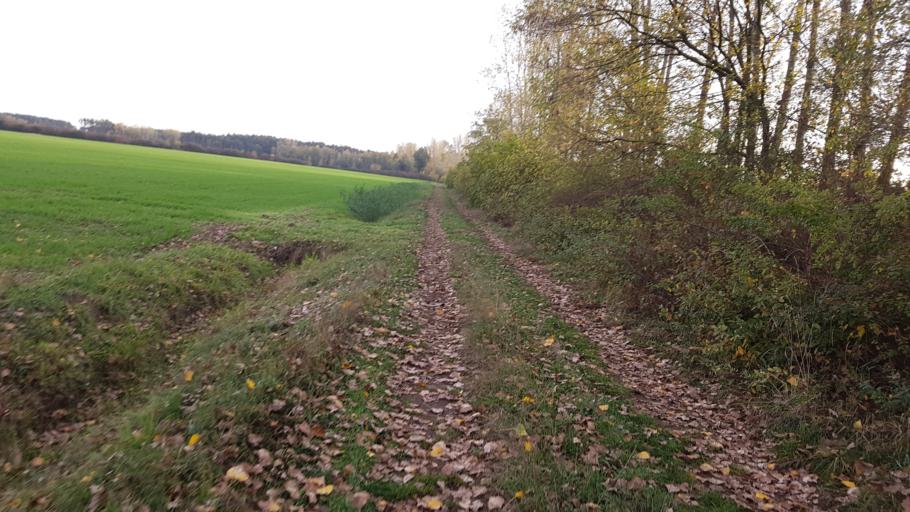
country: DE
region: Brandenburg
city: Schilda
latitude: 51.5655
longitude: 13.4059
